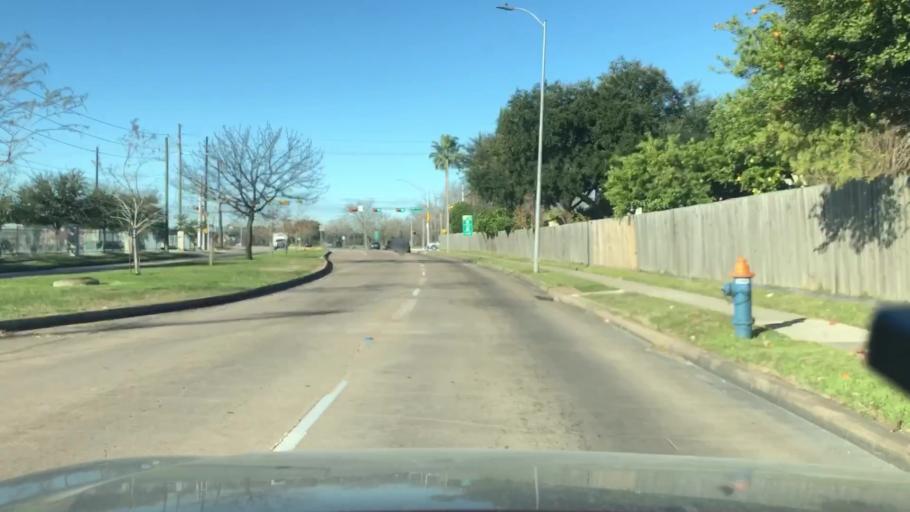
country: US
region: Texas
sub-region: Fort Bend County
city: Missouri City
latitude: 29.6456
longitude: -95.5349
